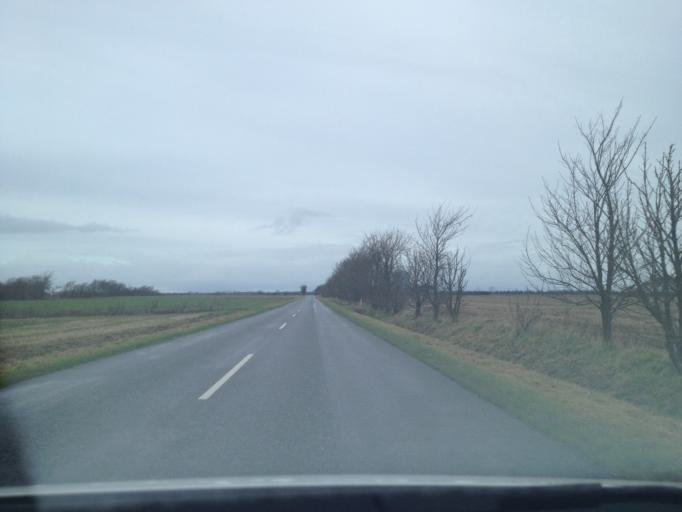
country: DK
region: South Denmark
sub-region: Tonder Kommune
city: Sherrebek
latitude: 55.2183
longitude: 8.8306
